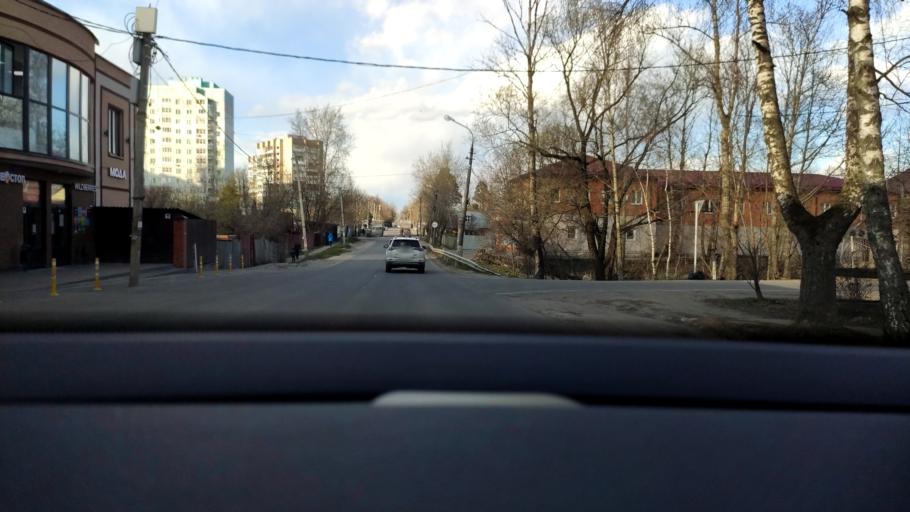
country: RU
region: Moskovskaya
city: Saltykovka
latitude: 55.7741
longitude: 37.8991
